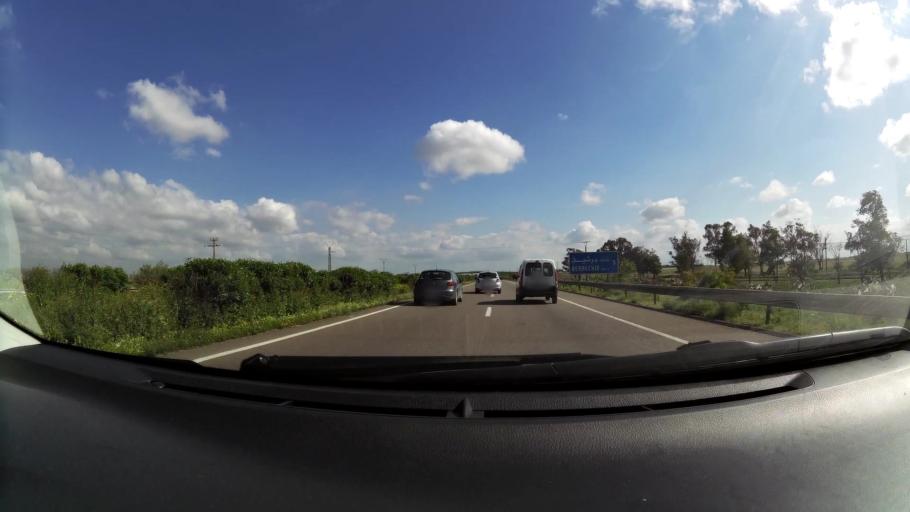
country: MA
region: Chaouia-Ouardigha
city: Nouaseur
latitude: 33.3623
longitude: -7.6196
